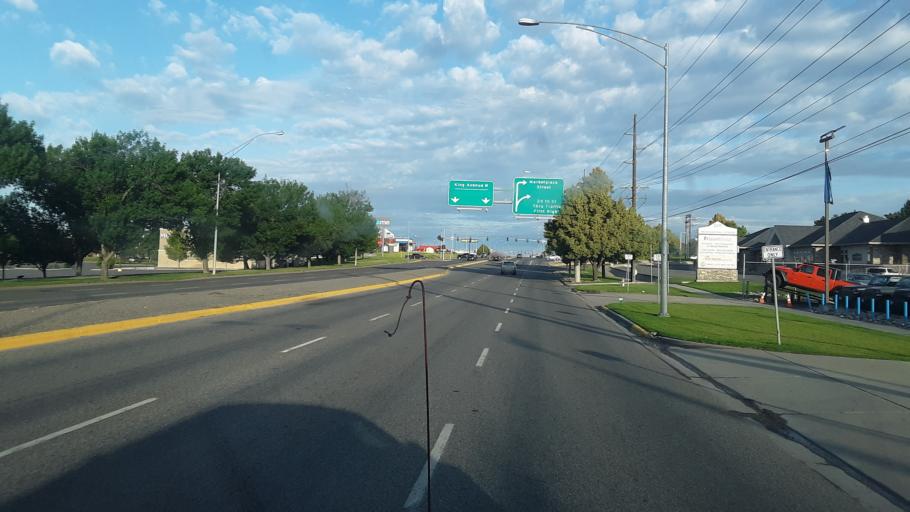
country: US
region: Montana
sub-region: Yellowstone County
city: Billings
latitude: 45.7552
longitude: -108.5733
